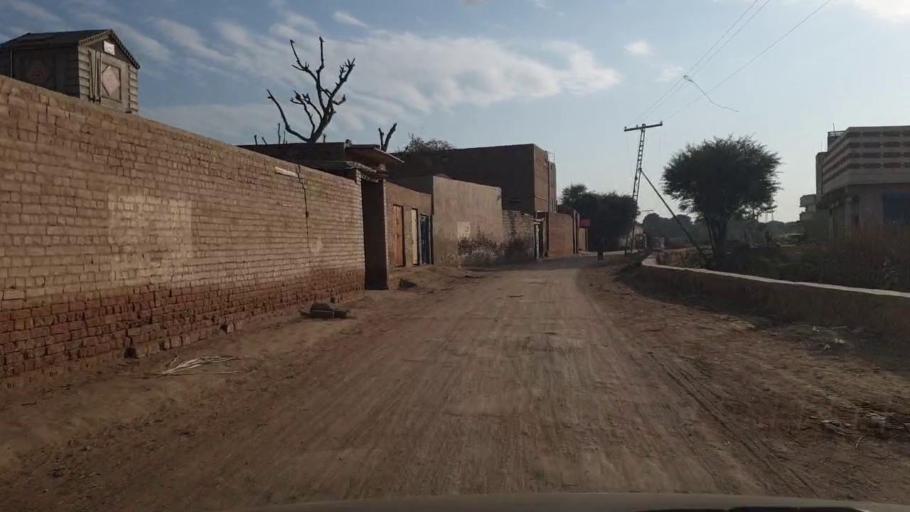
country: PK
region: Sindh
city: Sakrand
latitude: 26.0226
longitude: 68.3562
